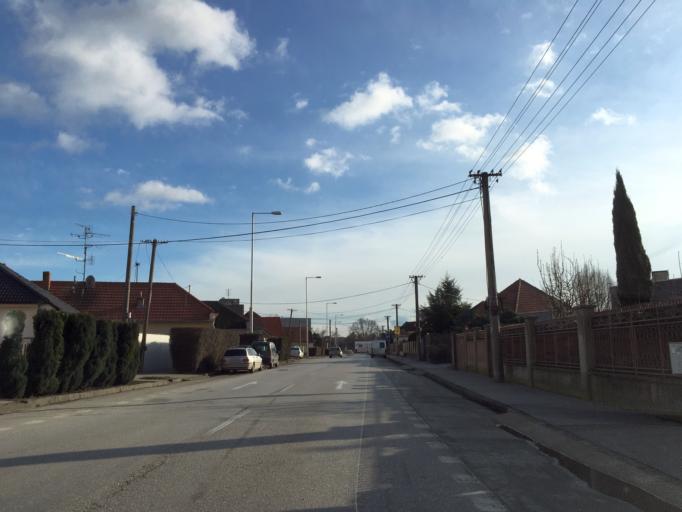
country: SK
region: Nitriansky
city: Sellye
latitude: 48.1545
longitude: 17.8671
